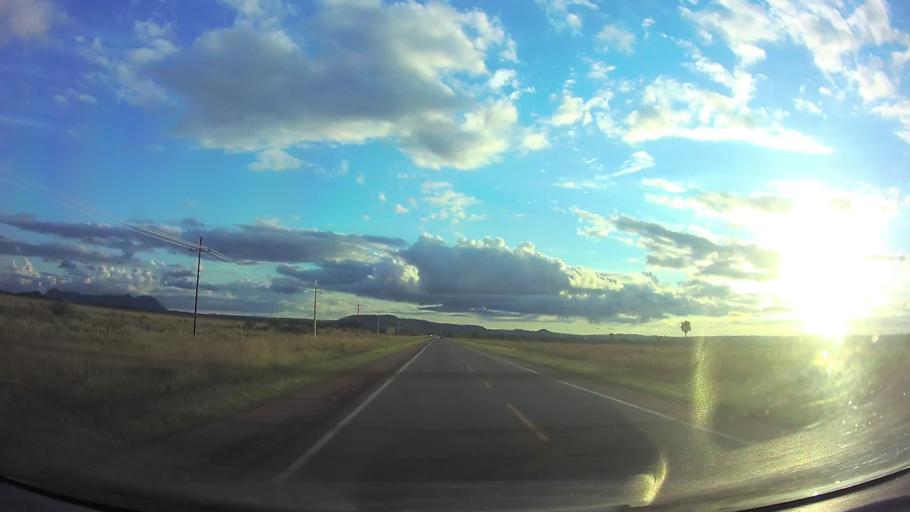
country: PY
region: Paraguari
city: Carapegua
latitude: -25.7366
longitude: -57.2098
